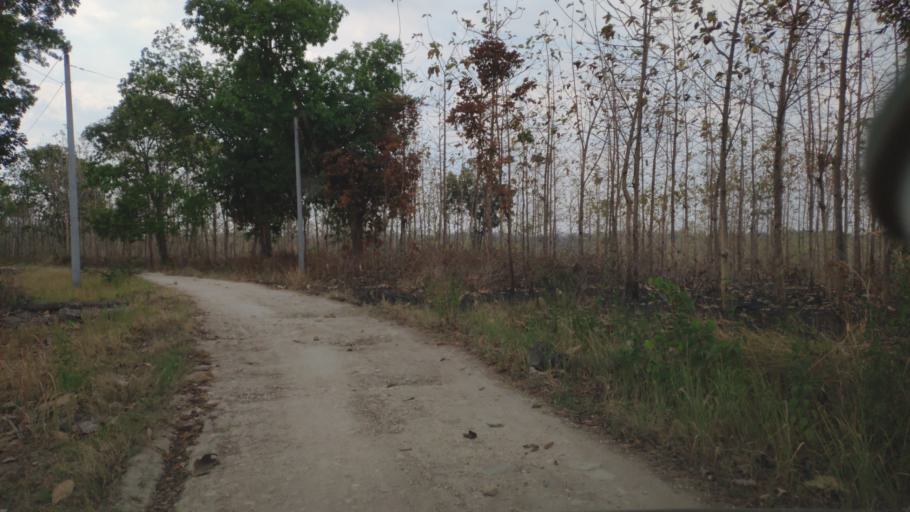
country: ID
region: Central Java
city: Randublatung
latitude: -7.2891
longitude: 111.3308
